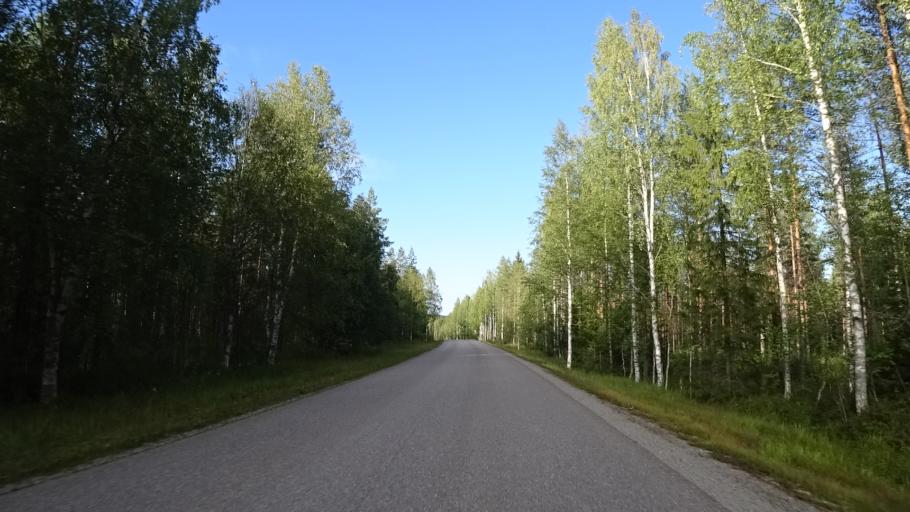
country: FI
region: North Karelia
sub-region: Joensuu
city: Eno
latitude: 63.0151
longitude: 30.4880
